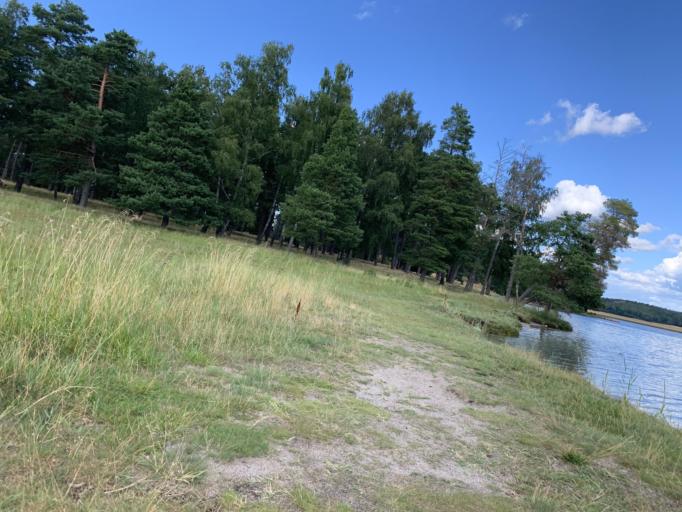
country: SE
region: Stockholm
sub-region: Sodertalje Kommun
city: Pershagen
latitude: 59.1021
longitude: 17.6822
